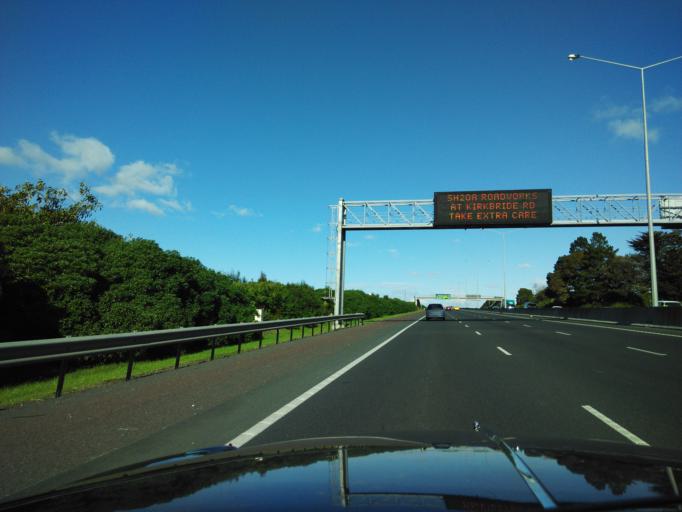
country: NZ
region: Auckland
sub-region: Auckland
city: Mangere
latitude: -36.9426
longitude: 174.7917
